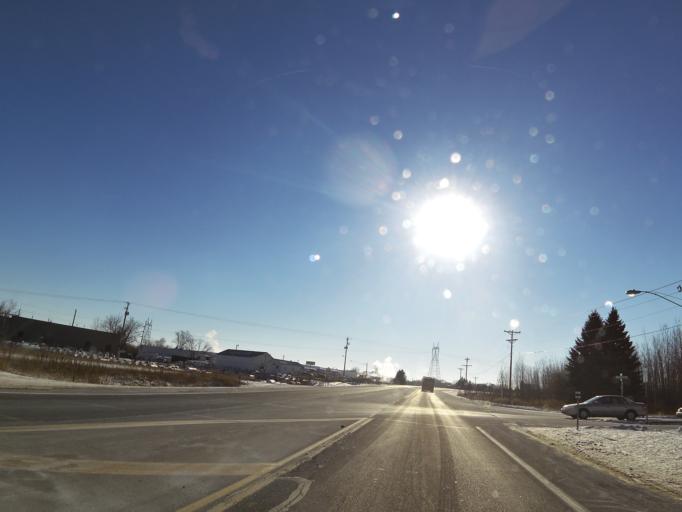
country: US
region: Minnesota
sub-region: Carver County
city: Chaska
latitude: 44.8062
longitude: -93.5741
